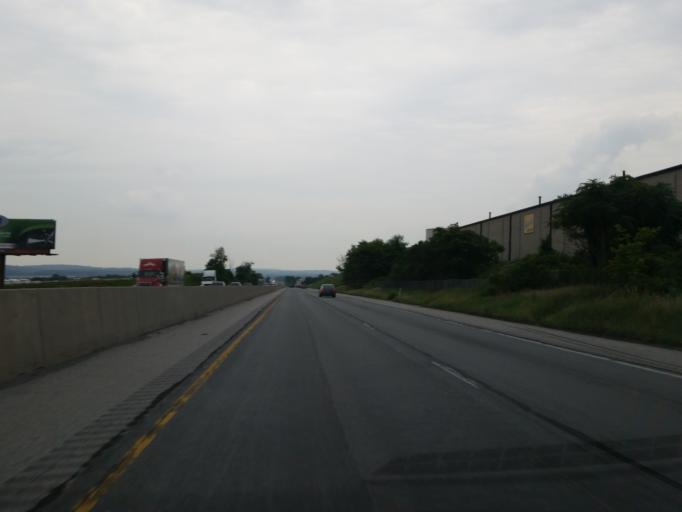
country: US
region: Pennsylvania
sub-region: York County
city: Emigsville
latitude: 40.0321
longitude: -76.7459
